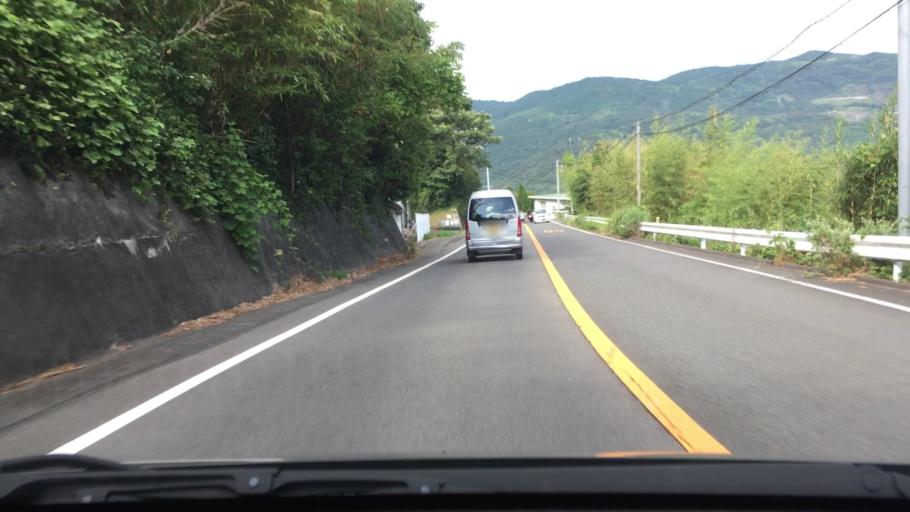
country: JP
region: Nagasaki
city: Togitsu
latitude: 32.8367
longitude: 129.7073
